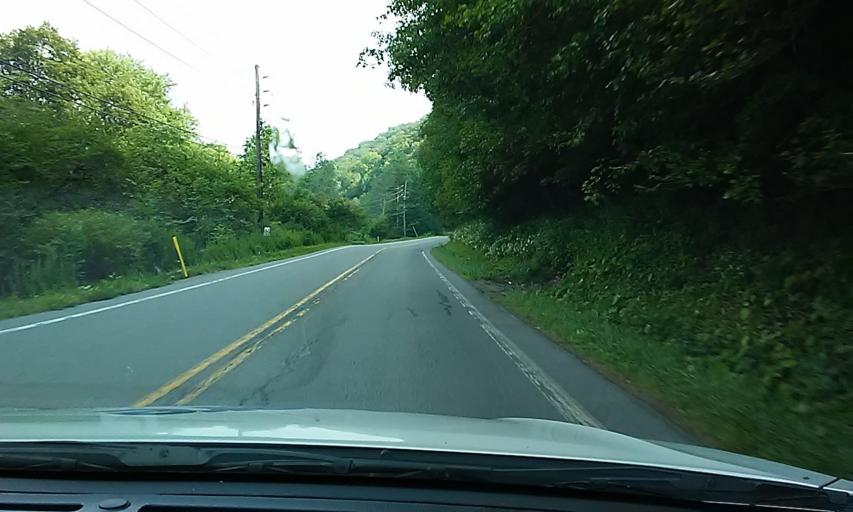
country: US
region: Pennsylvania
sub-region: Potter County
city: Galeton
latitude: 41.8123
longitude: -77.7861
